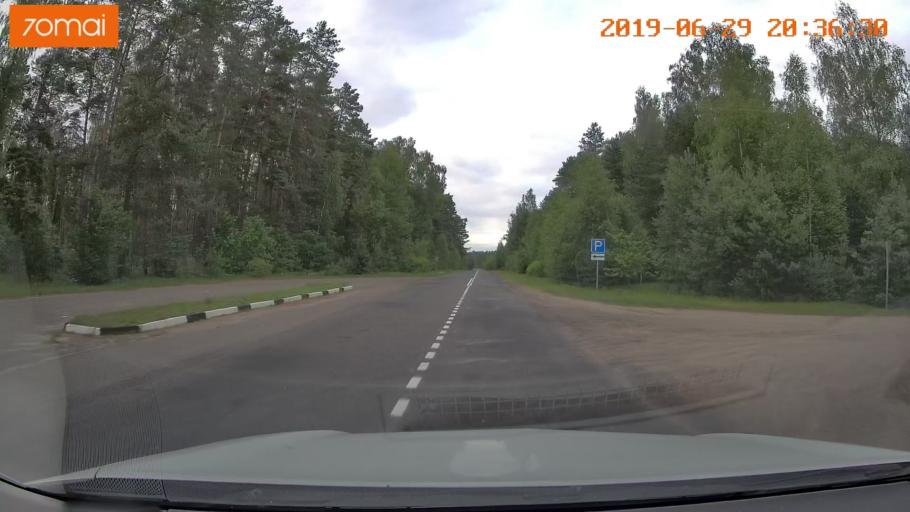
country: BY
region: Brest
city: Hantsavichy
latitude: 52.5269
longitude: 26.3590
